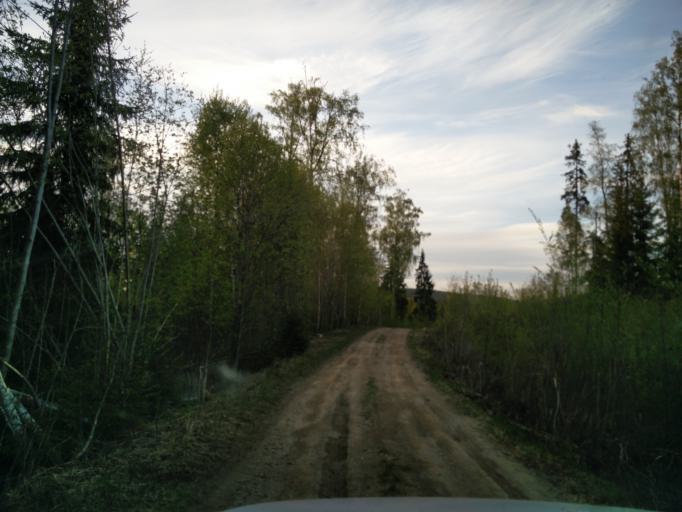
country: SE
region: Vaesternorrland
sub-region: Sundsvalls Kommun
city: Matfors
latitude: 62.3948
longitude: 16.8144
